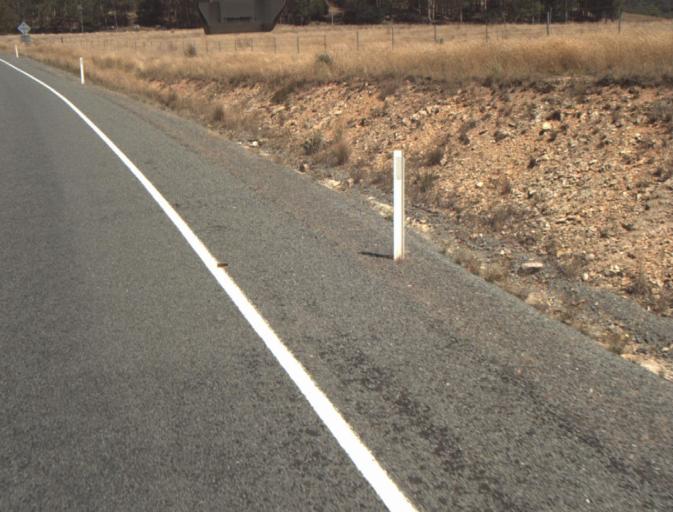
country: AU
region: Tasmania
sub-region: Launceston
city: Newstead
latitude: -41.3321
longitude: 147.3503
